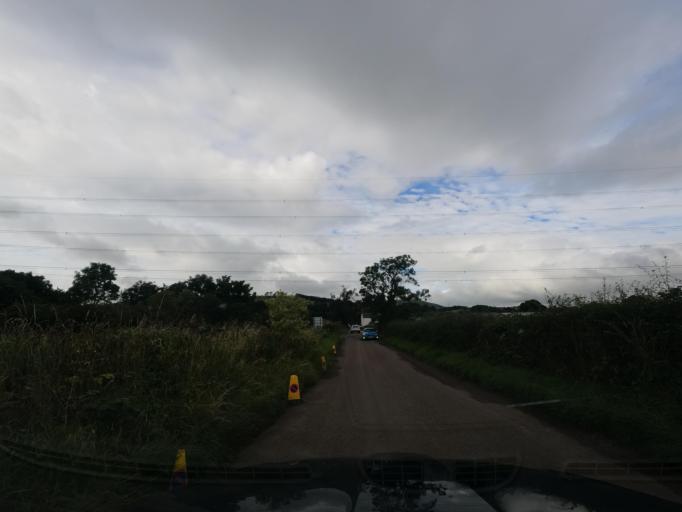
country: GB
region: England
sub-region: Northumberland
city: Wooler
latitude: 55.5444
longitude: -2.0014
